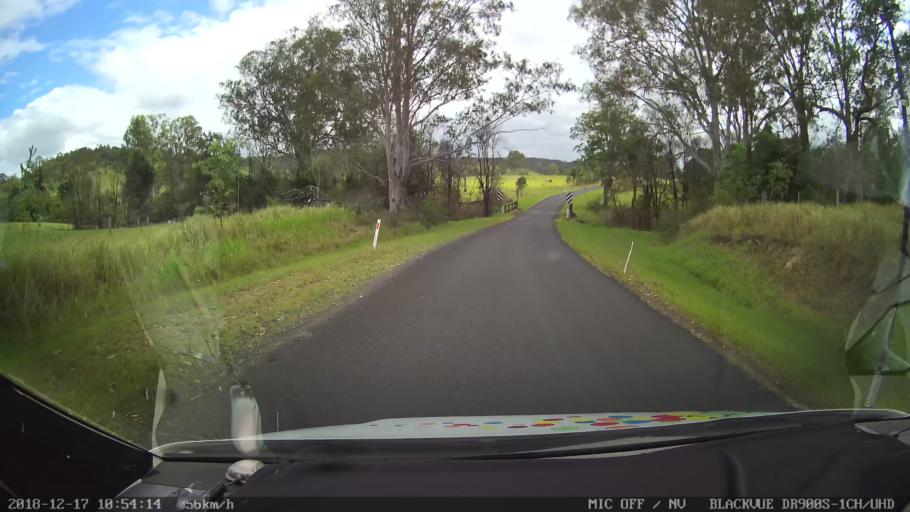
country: AU
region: New South Wales
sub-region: Tenterfield Municipality
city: Carrolls Creek
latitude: -28.8304
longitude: 152.5659
